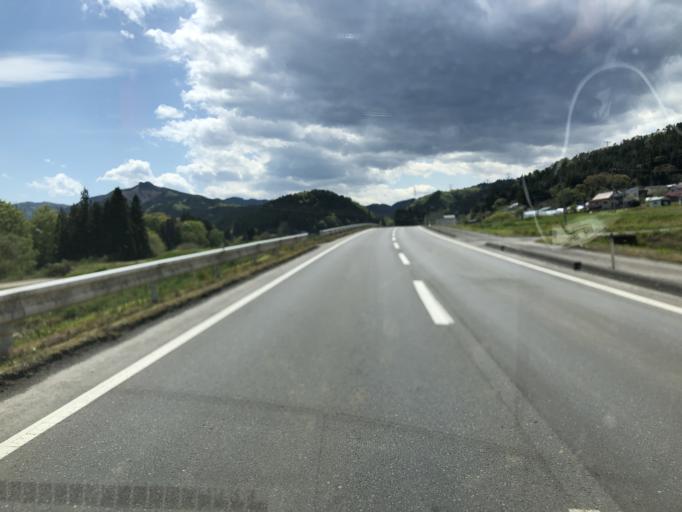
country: JP
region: Fukushima
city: Ishikawa
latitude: 37.0104
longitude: 140.3373
